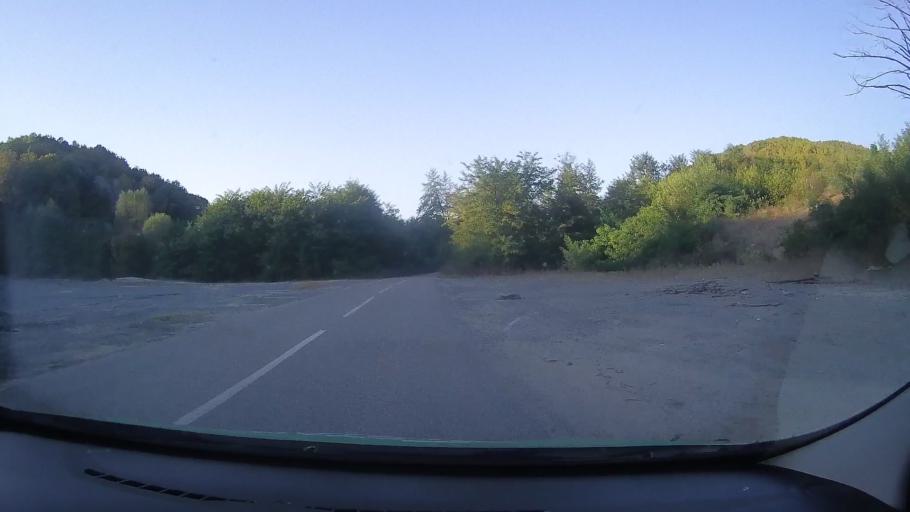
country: RO
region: Timis
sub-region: Comuna Fardea
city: Fardea
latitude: 45.6948
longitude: 22.1600
